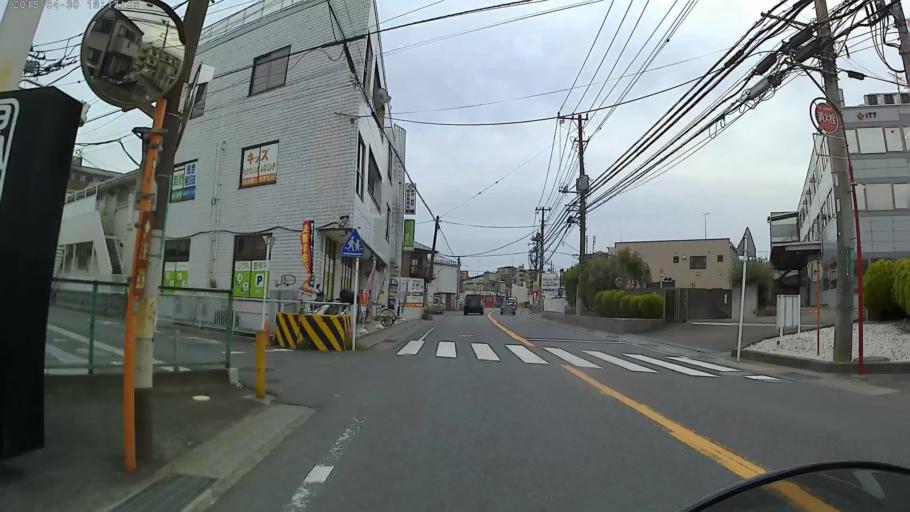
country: JP
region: Kanagawa
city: Minami-rinkan
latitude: 35.4918
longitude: 139.4312
